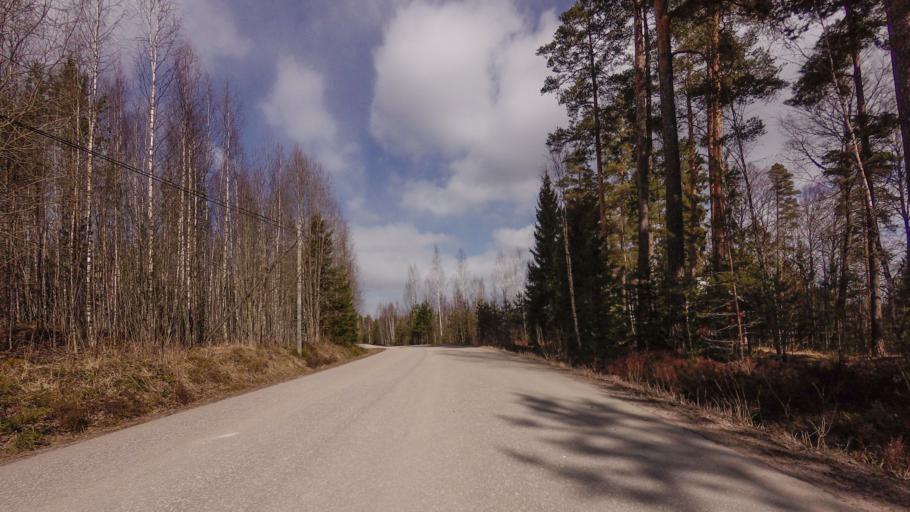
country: FI
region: Varsinais-Suomi
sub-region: Salo
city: Suomusjaervi
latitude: 60.3077
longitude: 23.6463
